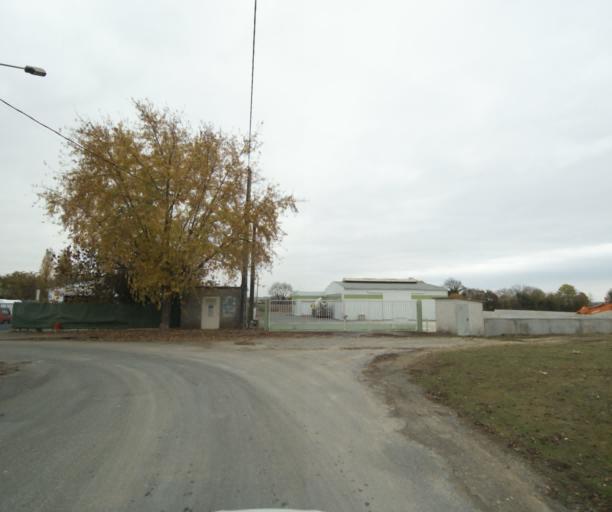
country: FR
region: Poitou-Charentes
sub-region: Departement de la Charente-Maritime
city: Les Gonds
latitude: 45.7192
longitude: -0.6386
